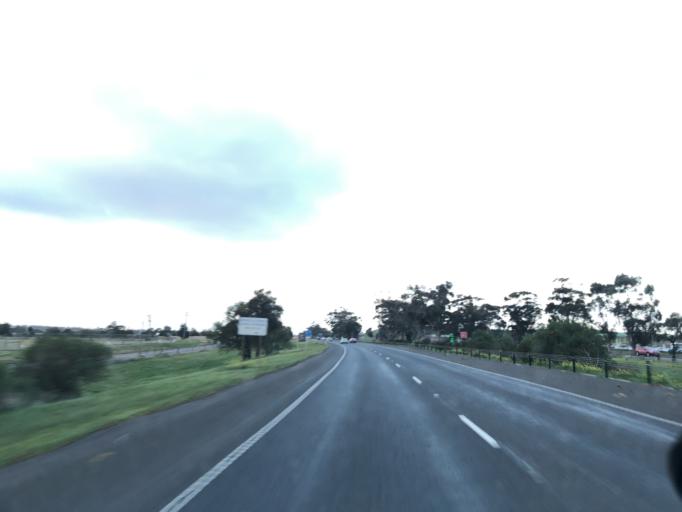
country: AU
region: Victoria
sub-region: Melton
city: Hillside
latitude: -37.6623
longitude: 144.7462
